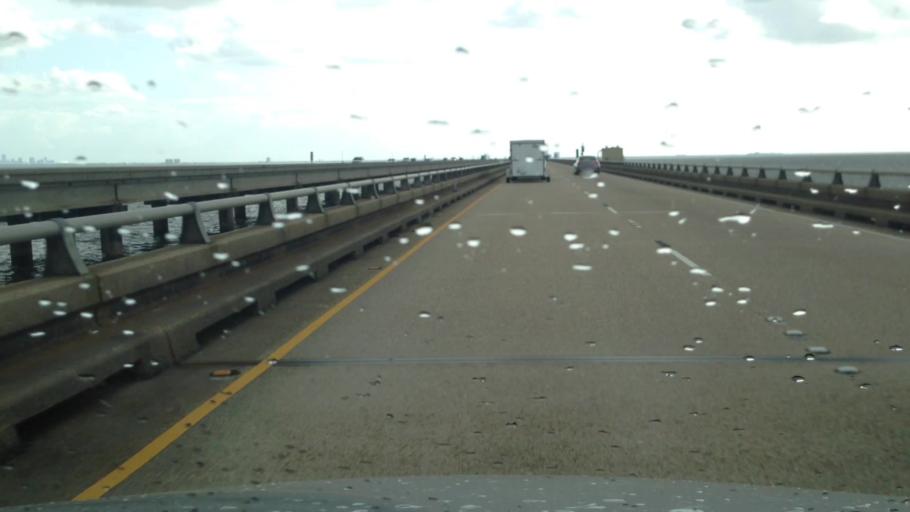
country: US
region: Louisiana
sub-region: Jefferson Parish
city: Metairie
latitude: 30.1109
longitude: -90.1385
